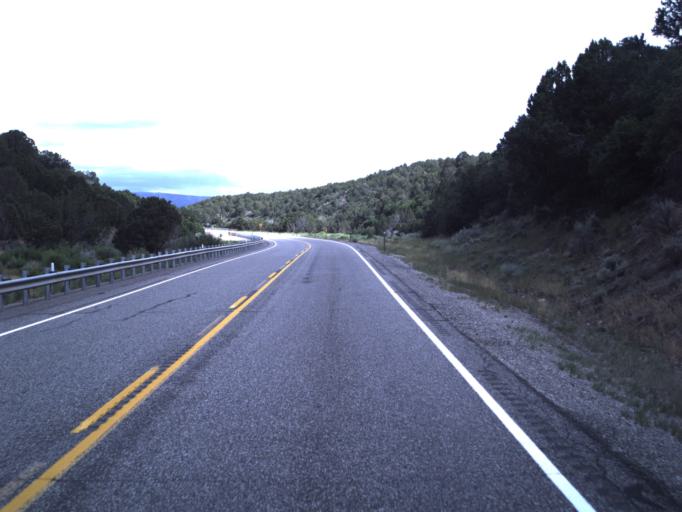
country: US
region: Utah
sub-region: Sevier County
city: Richfield
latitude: 38.7162
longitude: -111.9035
